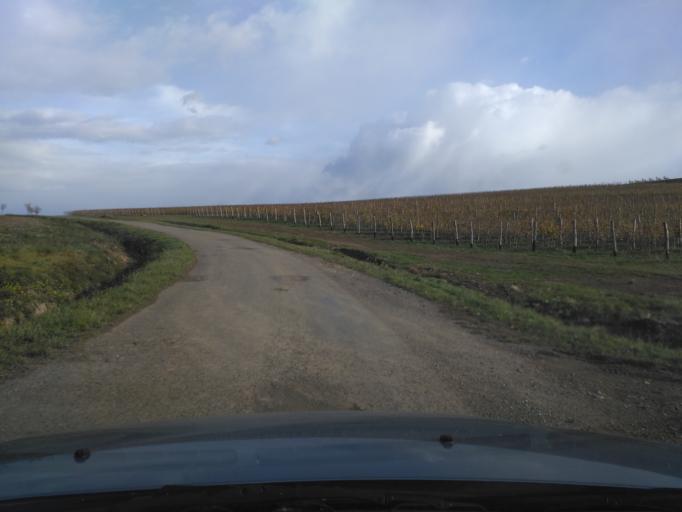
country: HU
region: Borsod-Abauj-Zemplen
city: Satoraljaujhely
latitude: 48.4385
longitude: 21.7096
